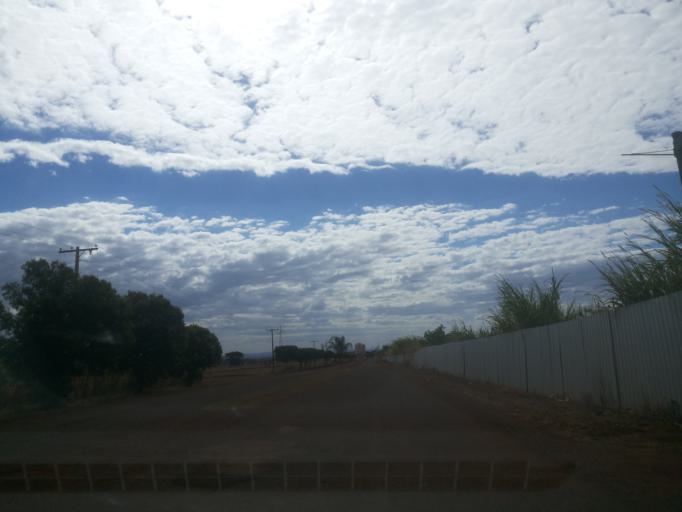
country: BR
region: Minas Gerais
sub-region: Centralina
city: Centralina
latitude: -18.6038
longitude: -49.1943
